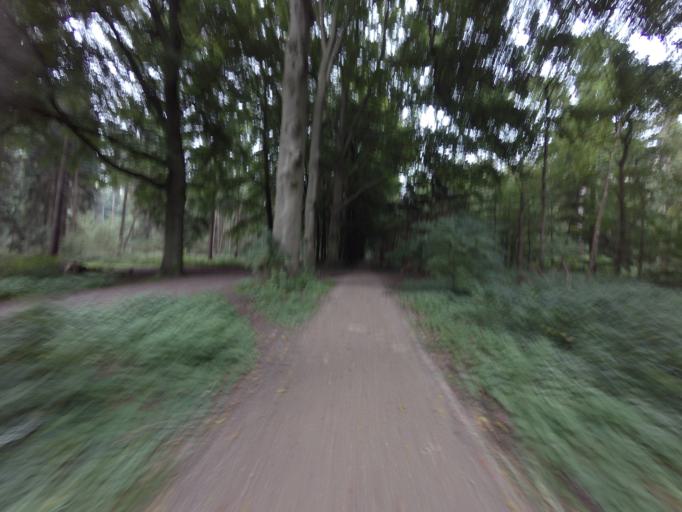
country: NL
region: Utrecht
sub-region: Gemeente Baarn
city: Baarn
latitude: 52.2051
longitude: 5.2360
